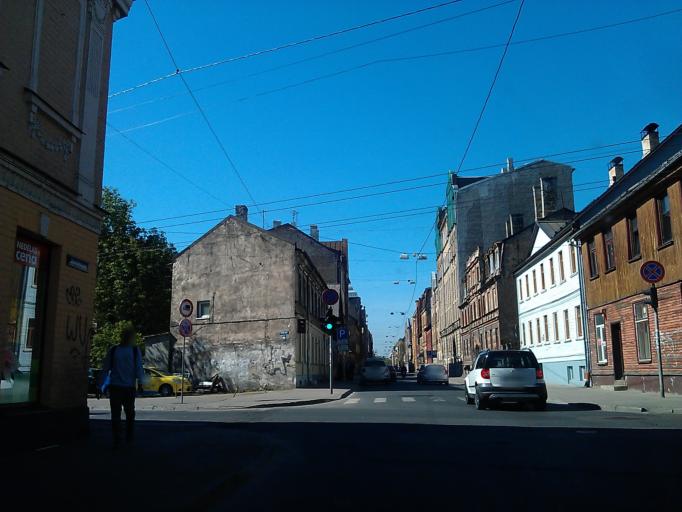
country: LV
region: Riga
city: Riga
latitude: 56.9520
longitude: 24.1399
